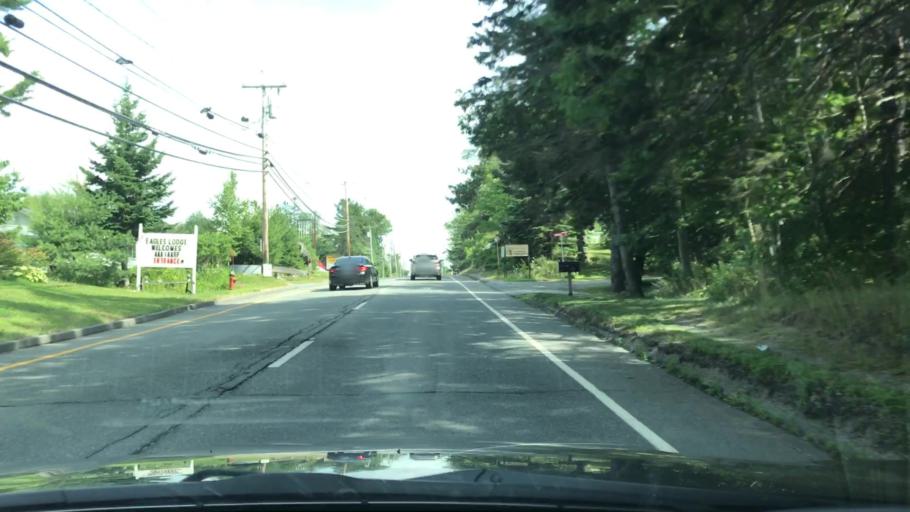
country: US
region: Maine
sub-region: Hancock County
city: Ellsworth
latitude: 44.5288
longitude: -68.4037
